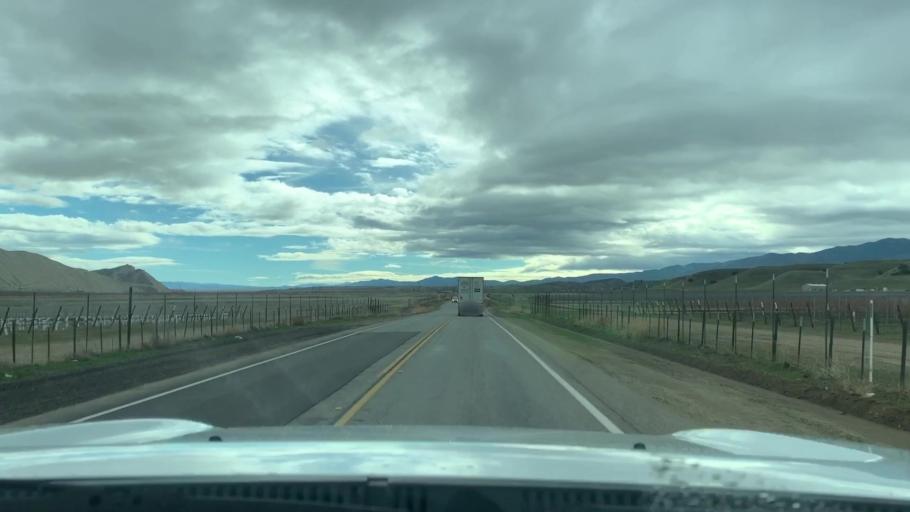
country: US
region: California
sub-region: Kern County
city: Taft Heights
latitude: 35.0226
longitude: -119.8595
